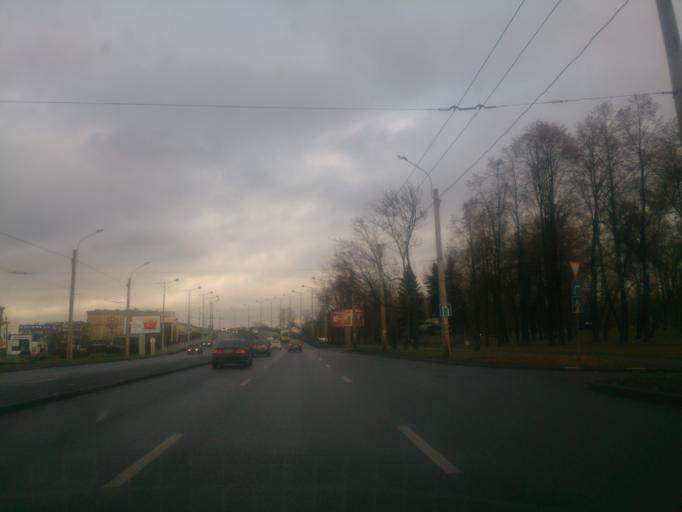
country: RU
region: St.-Petersburg
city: Avtovo
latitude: 59.8605
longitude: 30.2570
